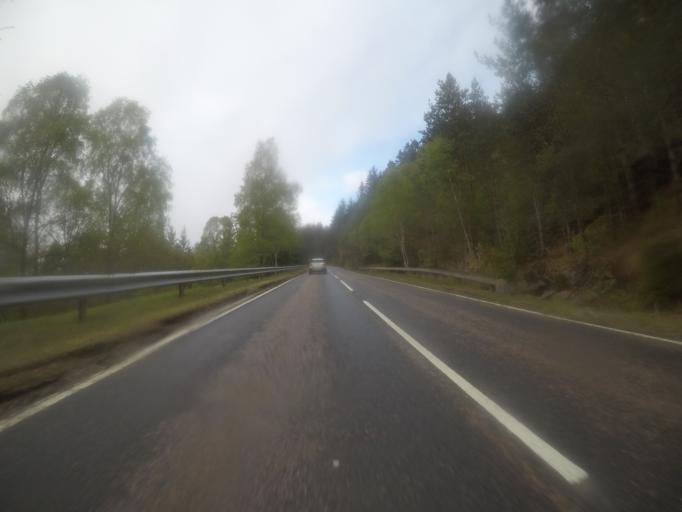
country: GB
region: Scotland
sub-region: Highland
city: Spean Bridge
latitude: 57.0831
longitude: -4.9307
